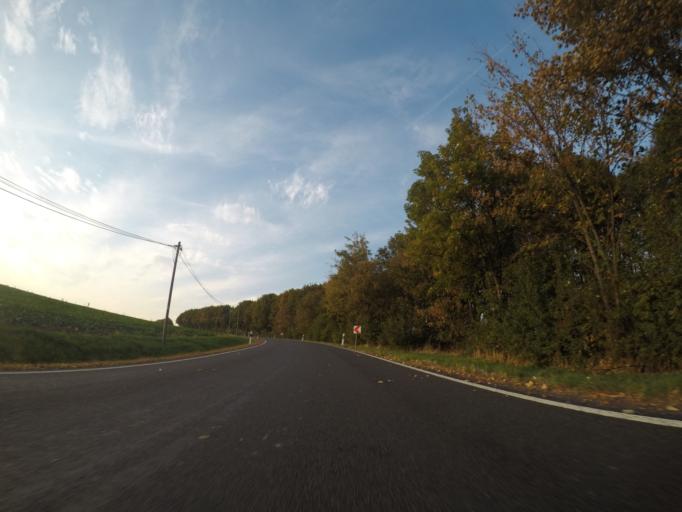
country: DE
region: Thuringia
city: Altkirchen
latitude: 50.9232
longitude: 12.3352
